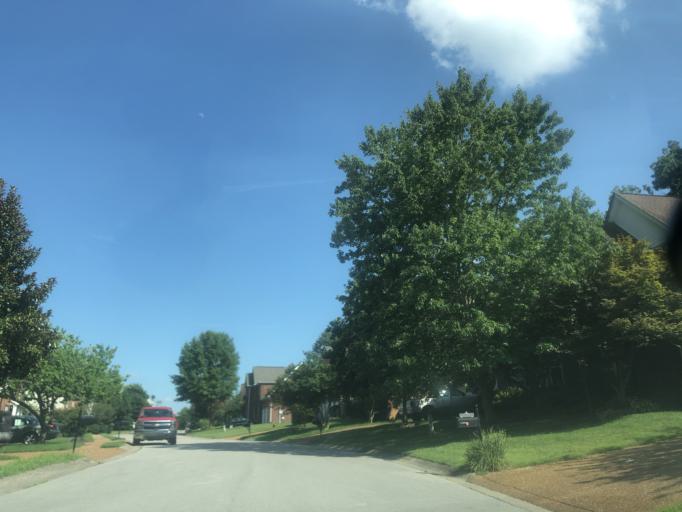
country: US
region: Tennessee
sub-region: Wilson County
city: Green Hill
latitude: 36.1513
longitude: -86.5891
